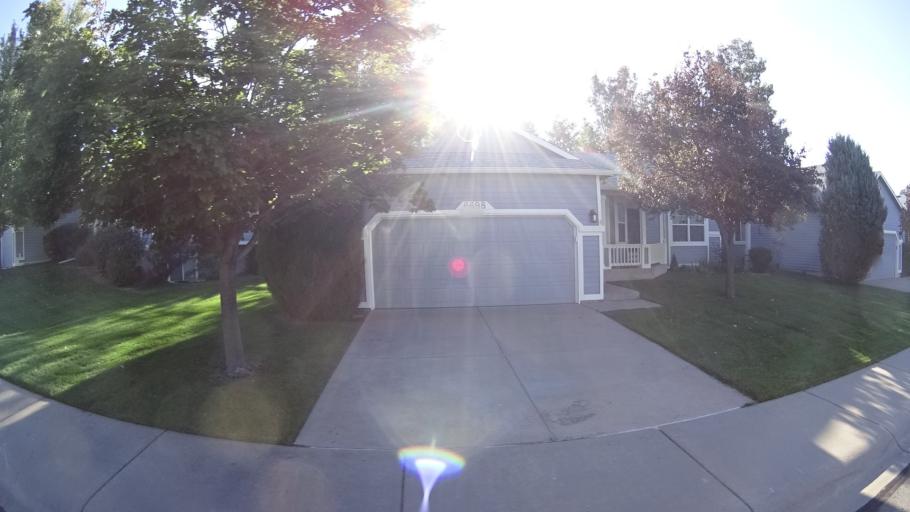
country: US
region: Colorado
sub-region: El Paso County
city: Cimarron Hills
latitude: 38.8908
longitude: -104.7069
